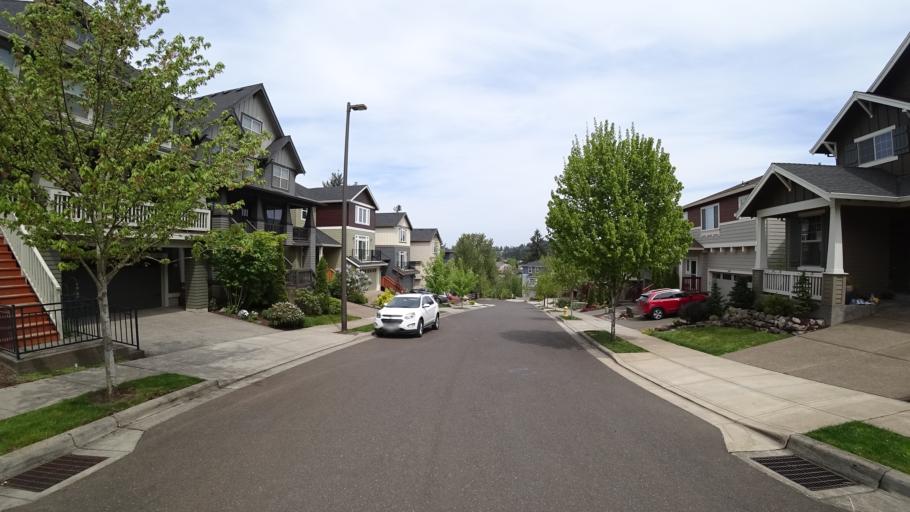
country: US
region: Oregon
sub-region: Washington County
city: Aloha
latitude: 45.4607
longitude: -122.8545
